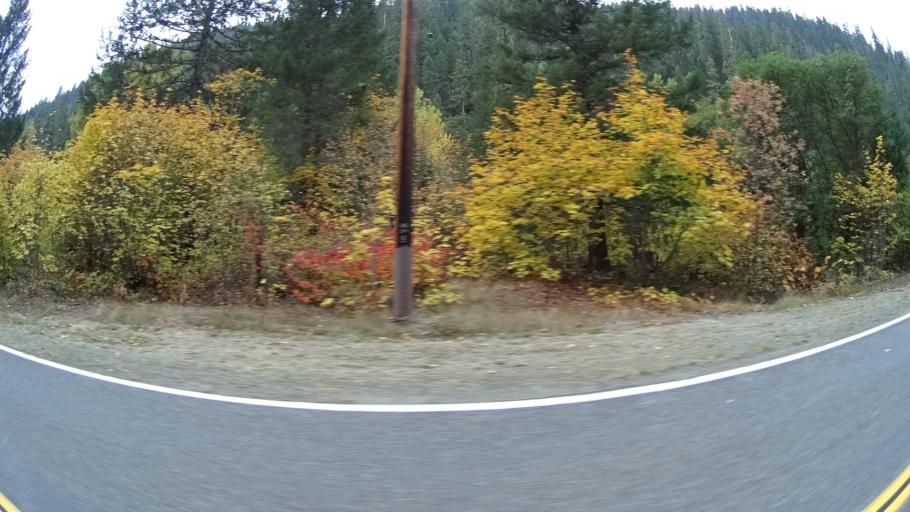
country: US
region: California
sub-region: Siskiyou County
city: Happy Camp
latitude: 41.8995
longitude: -123.4385
